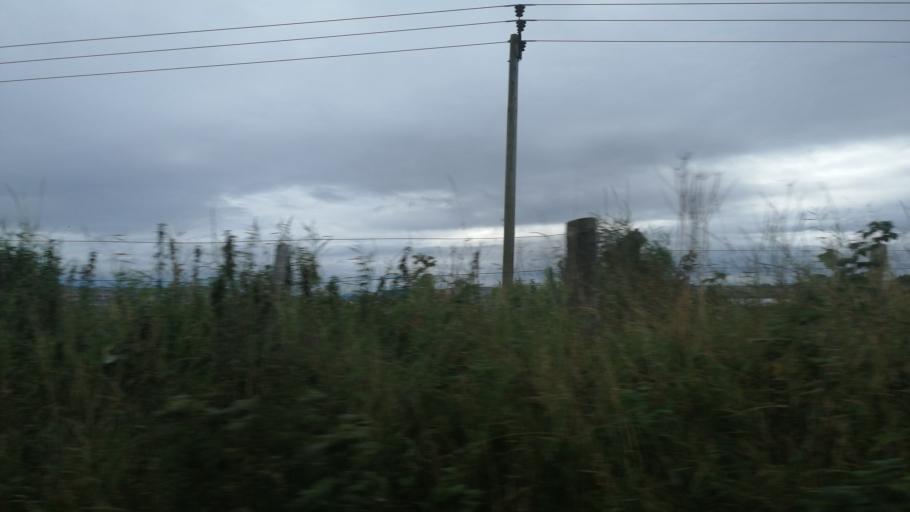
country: GB
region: Scotland
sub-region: Highland
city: Invergordon
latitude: 57.7237
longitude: -4.1112
